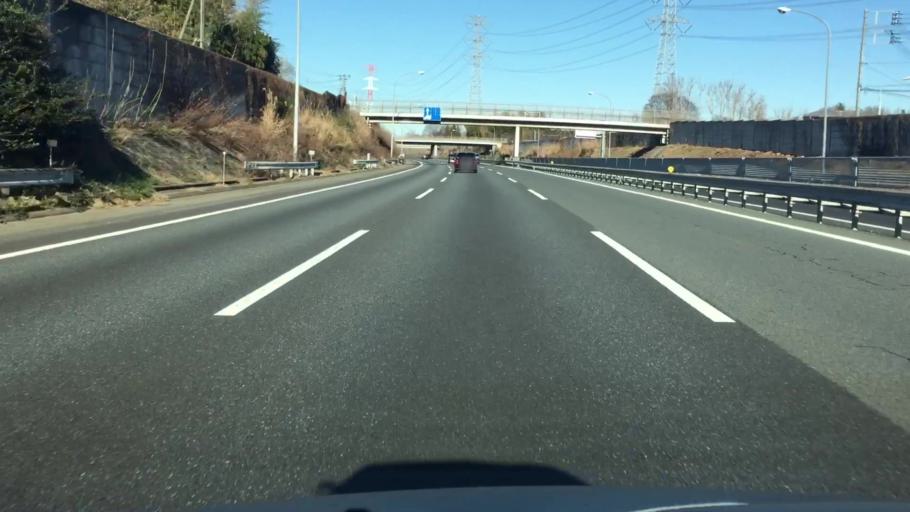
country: JP
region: Saitama
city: Sakado
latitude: 36.0332
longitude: 139.3792
